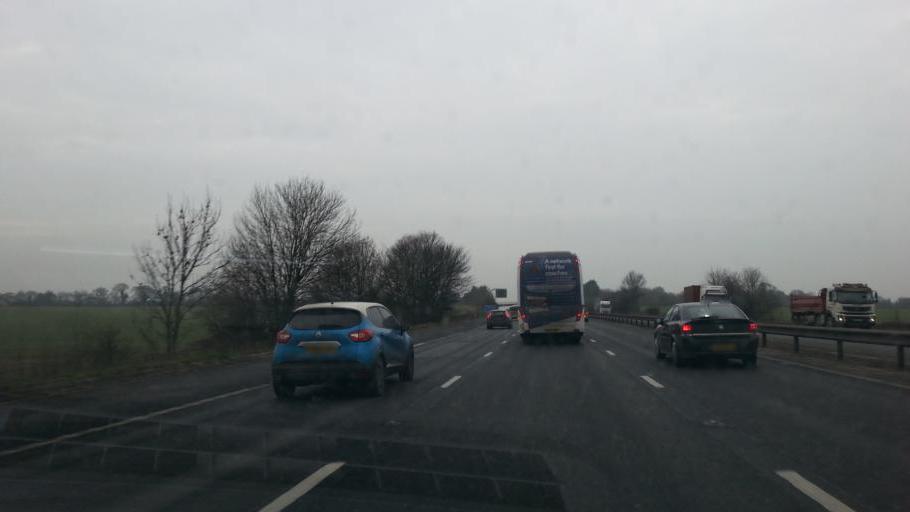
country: GB
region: England
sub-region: Hertfordshire
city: Sawbridgeworth
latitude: 51.7963
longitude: 0.1744
